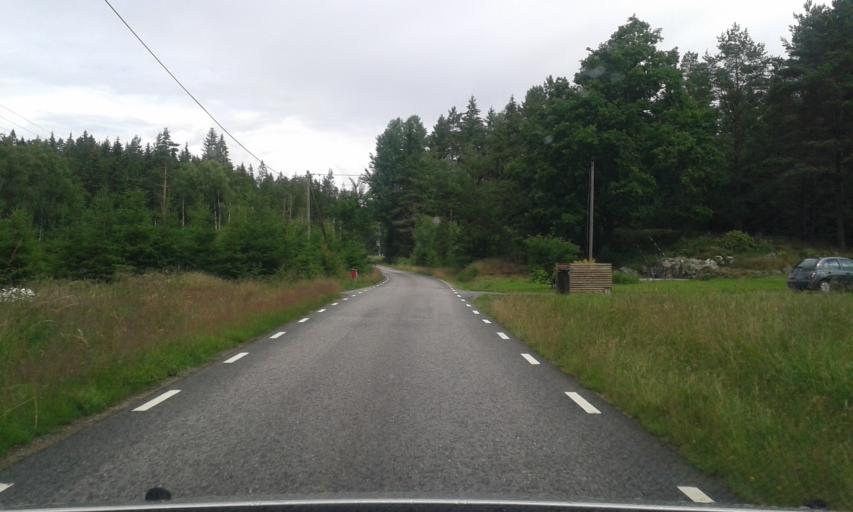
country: SE
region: Vaestra Goetaland
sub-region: Kungalvs Kommun
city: Diserod
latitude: 57.9629
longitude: 11.9619
